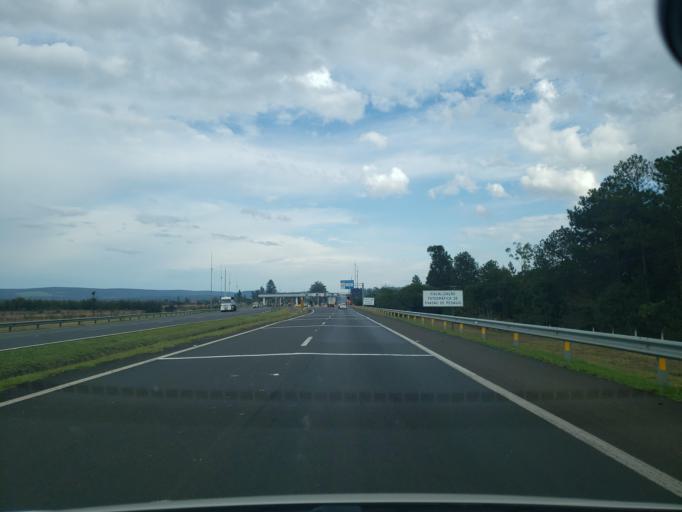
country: BR
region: Sao Paulo
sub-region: Itirapina
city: Itirapina
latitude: -22.2631
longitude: -47.8992
